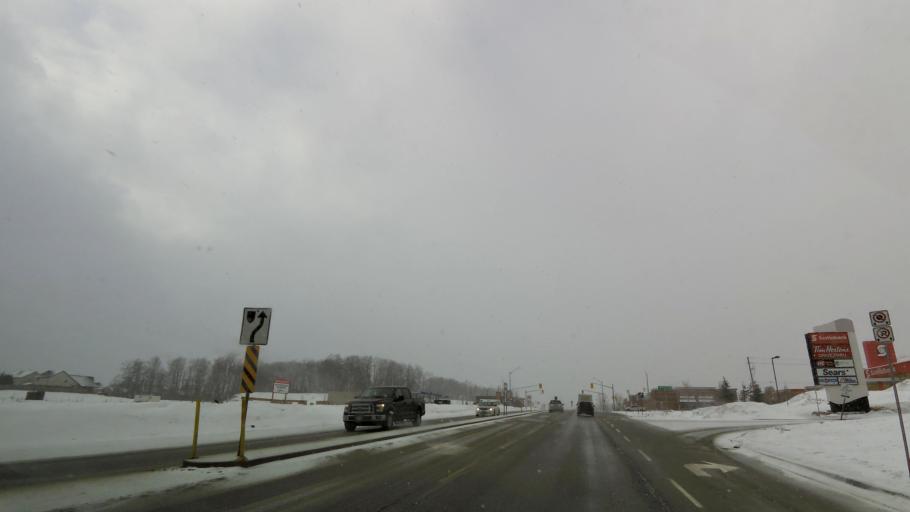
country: CA
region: Ontario
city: Orangeville
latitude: 43.9005
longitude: -80.1181
